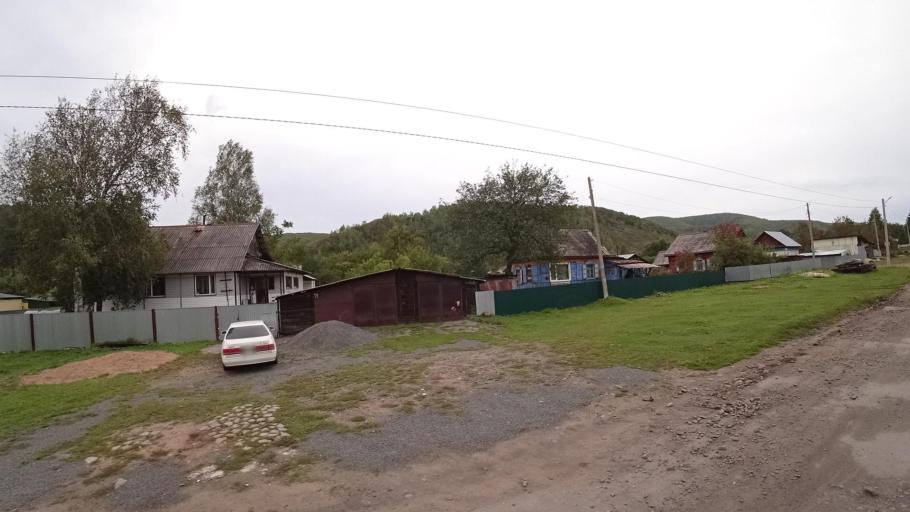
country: RU
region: Jewish Autonomous Oblast
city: Khingansk
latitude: 49.0250
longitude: 131.0480
